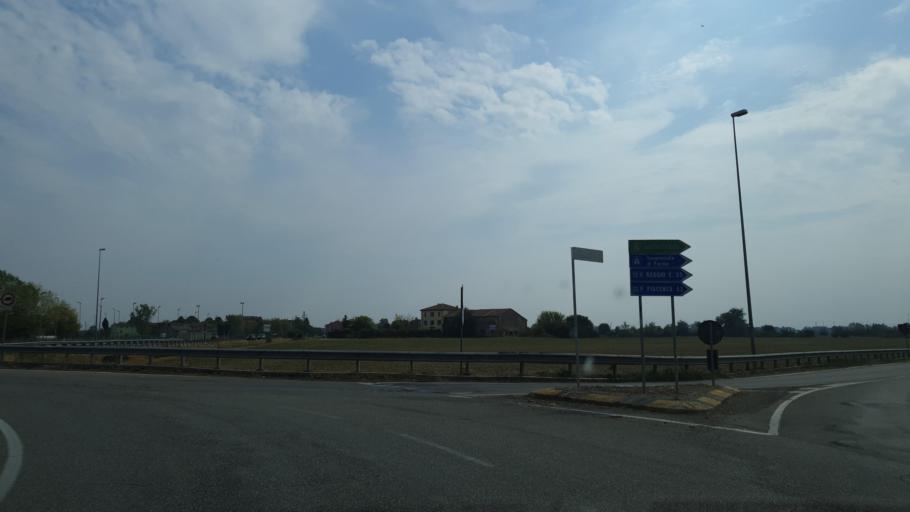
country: IT
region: Emilia-Romagna
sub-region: Provincia di Parma
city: Baganzola
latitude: 44.8298
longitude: 10.2747
